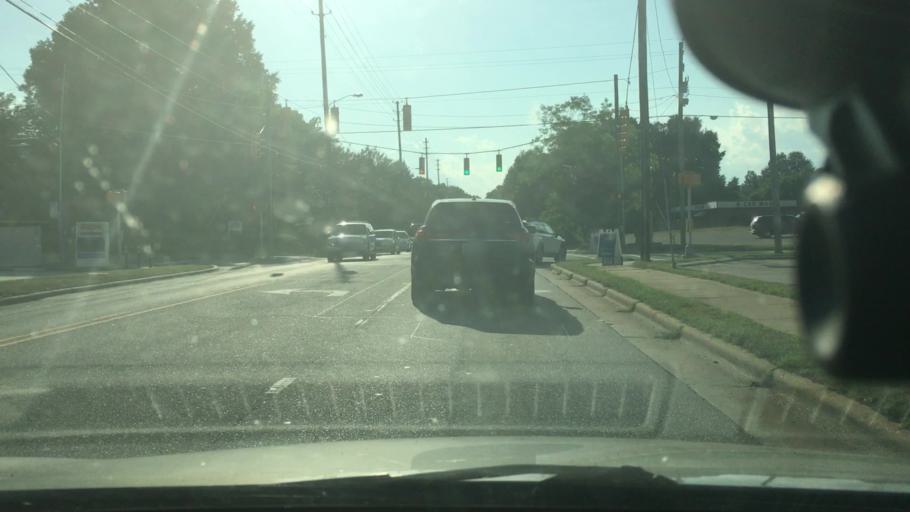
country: US
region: North Carolina
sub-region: Wake County
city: Apex
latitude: 35.7261
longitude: -78.8510
